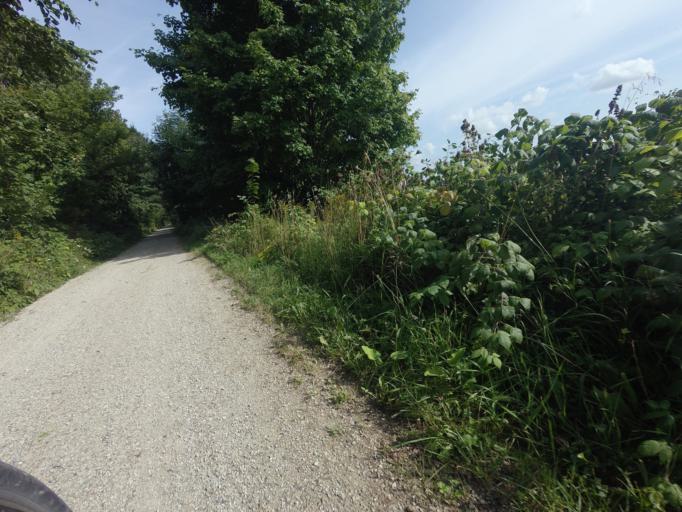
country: CA
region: Ontario
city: Waterloo
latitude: 43.5871
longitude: -80.4342
